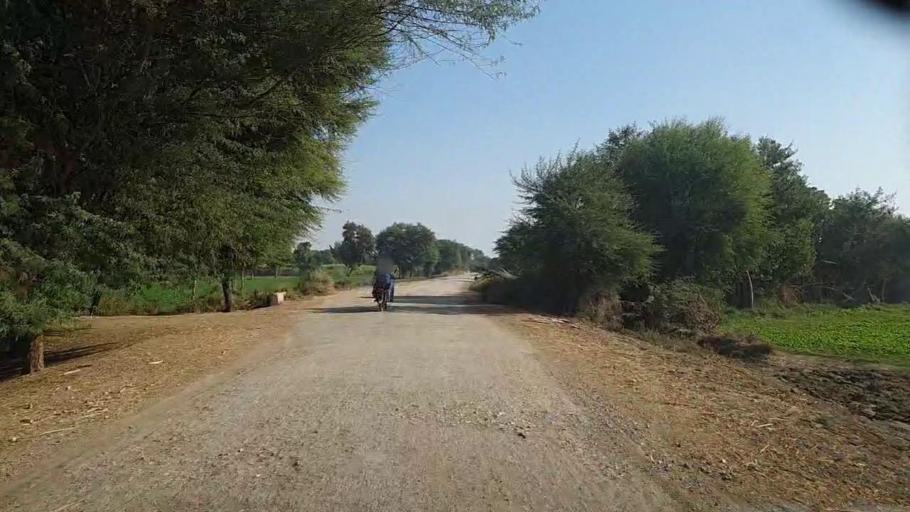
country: PK
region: Sindh
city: Darya Khan Marri
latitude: 26.6639
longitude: 68.3390
